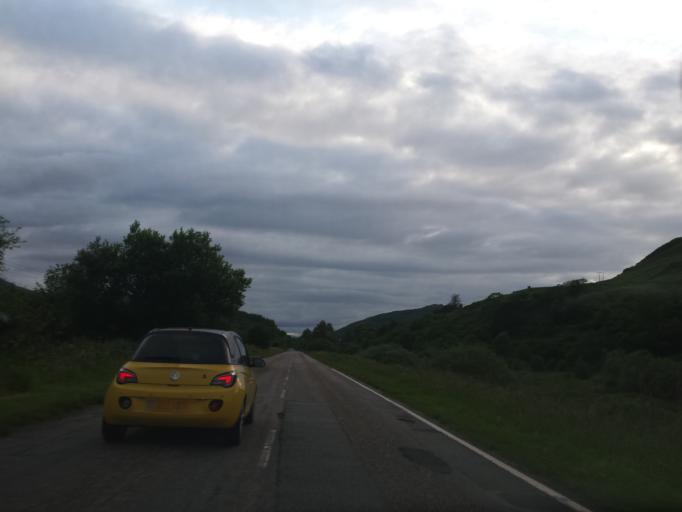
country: GB
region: Scotland
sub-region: Highland
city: Fort William
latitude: 57.2851
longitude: -5.5480
